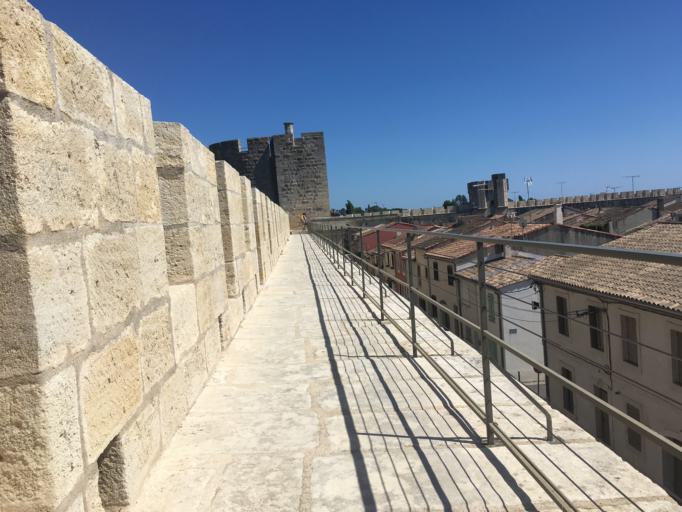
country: FR
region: Languedoc-Roussillon
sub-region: Departement du Gard
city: Aigues-Mortes
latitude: 43.5666
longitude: 4.1938
